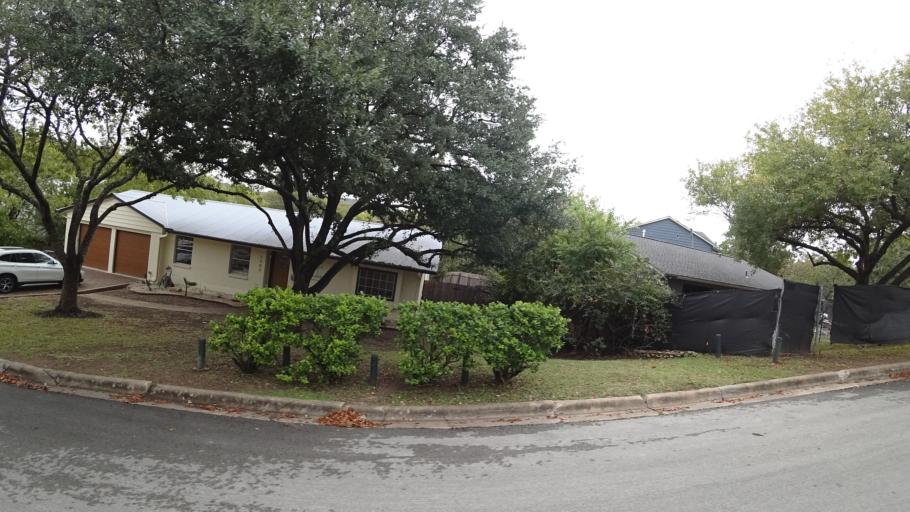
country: US
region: Texas
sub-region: Travis County
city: Rollingwood
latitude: 30.2505
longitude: -97.7839
